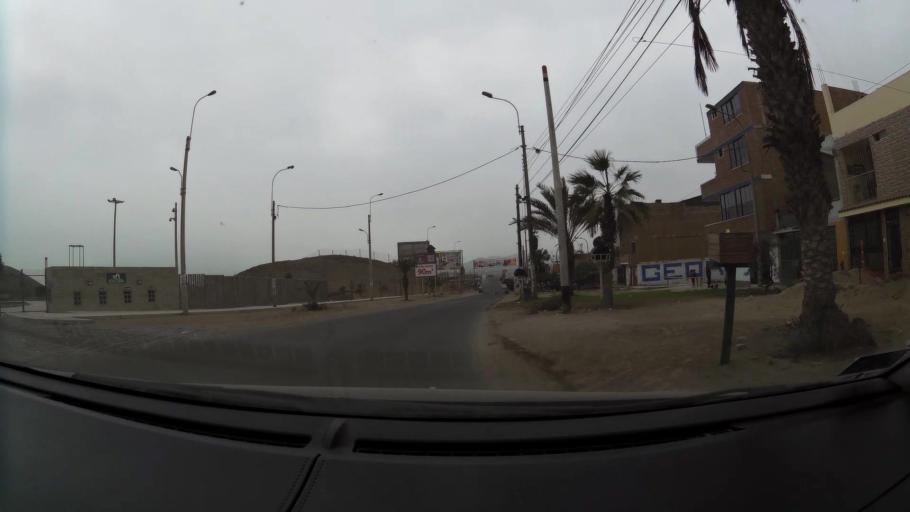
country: PE
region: Lima
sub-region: Lima
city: Santa Rosa
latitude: -11.7884
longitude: -77.1579
